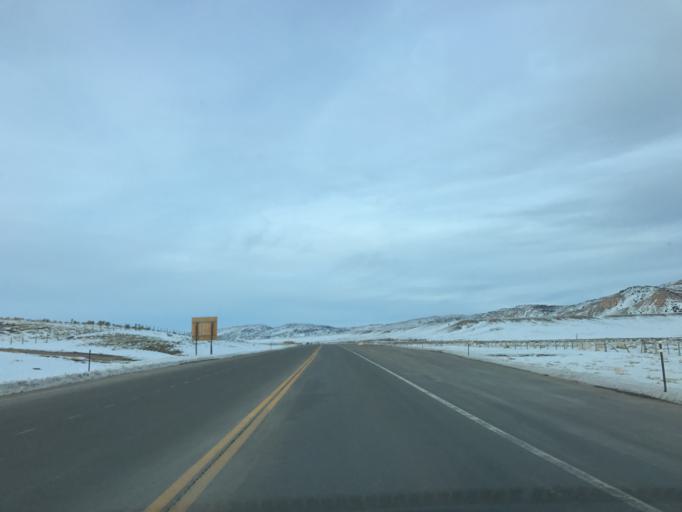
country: US
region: Wyoming
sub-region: Uinta County
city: Evanston
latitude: 41.3089
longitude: -110.7295
